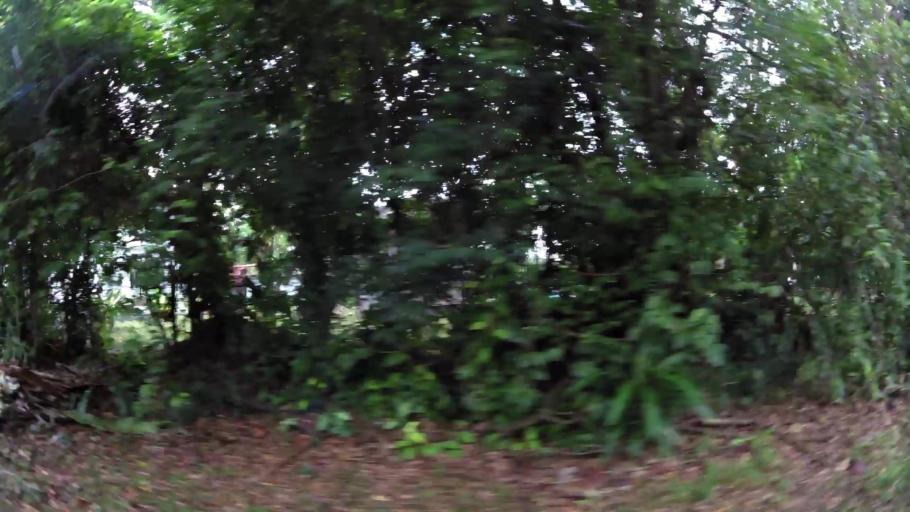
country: SG
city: Singapore
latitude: 1.2844
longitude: 103.7967
